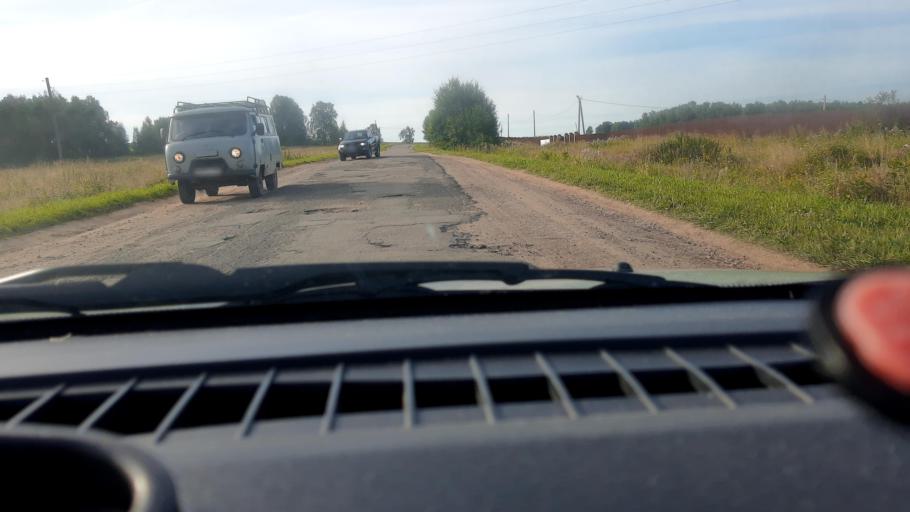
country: RU
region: Nizjnij Novgorod
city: Burevestnik
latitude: 56.0005
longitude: 43.9535
